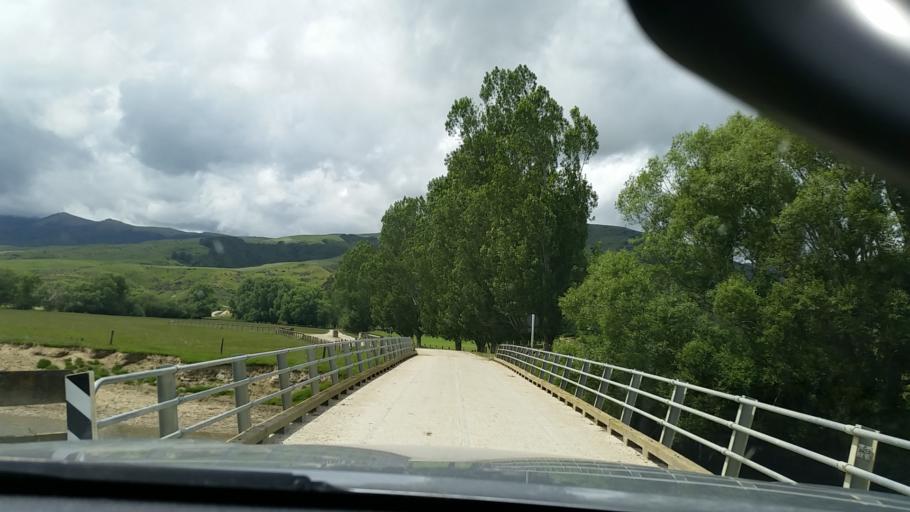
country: NZ
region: Otago
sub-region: Queenstown-Lakes District
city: Kingston
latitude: -45.6386
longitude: 168.9309
